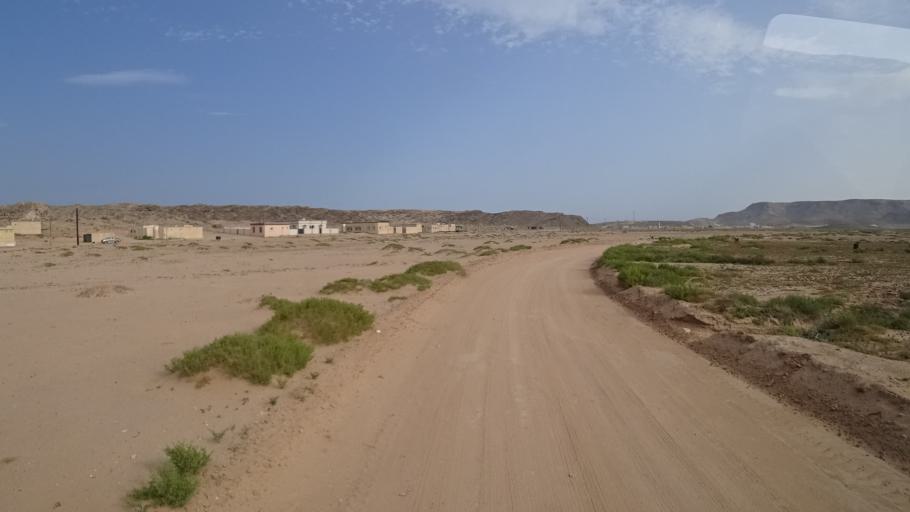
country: OM
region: Ash Sharqiyah
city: Sur
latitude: 22.4497
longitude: 59.8260
